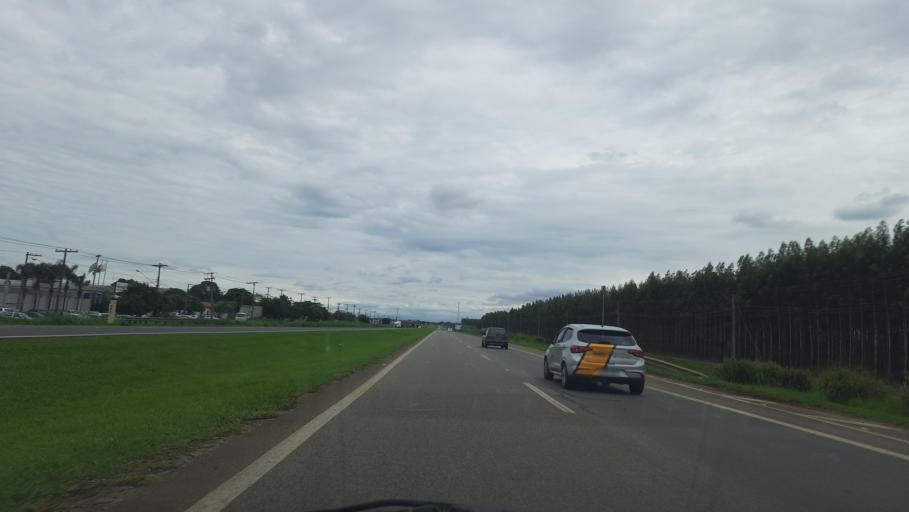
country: BR
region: Sao Paulo
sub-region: Moji-Guacu
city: Mogi-Gaucu
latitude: -22.3249
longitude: -46.9619
